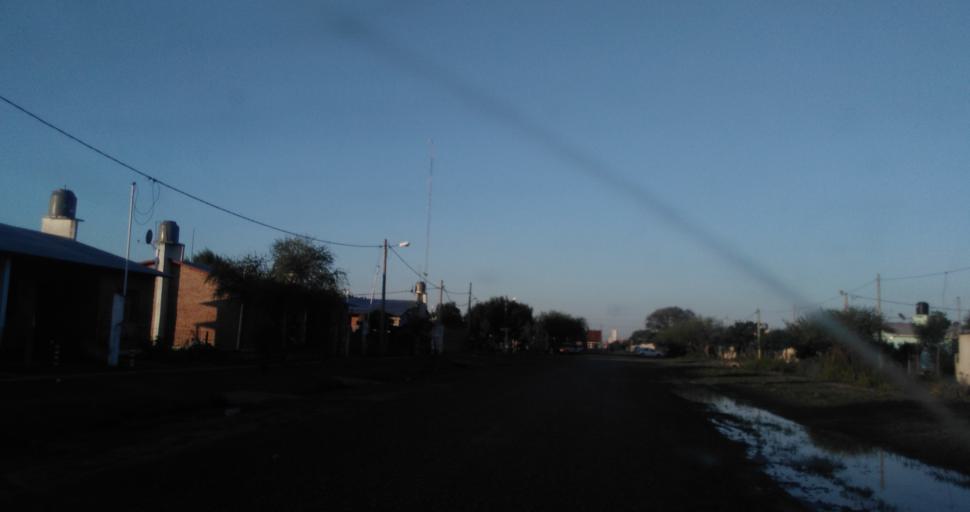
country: AR
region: Chaco
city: Resistencia
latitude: -27.4820
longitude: -59.0122
